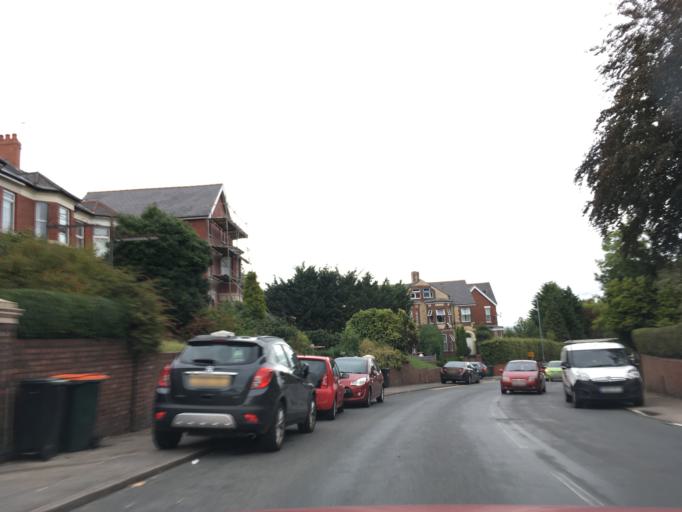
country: GB
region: Wales
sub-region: Newport
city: Newport
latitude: 51.5824
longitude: -3.0124
